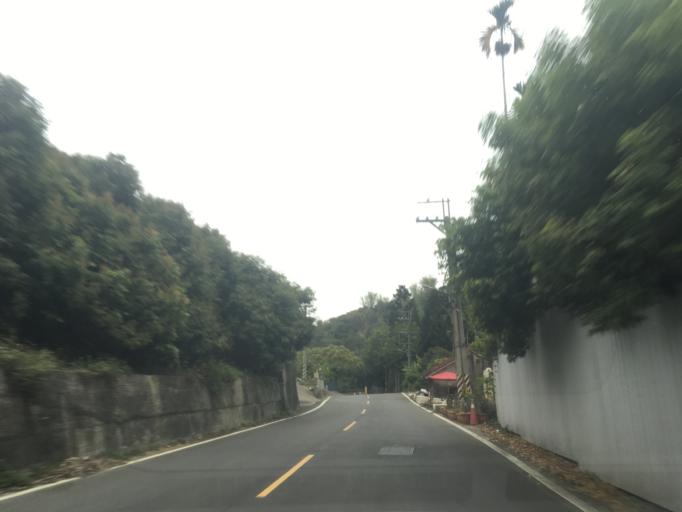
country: TW
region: Taiwan
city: Zhongxing New Village
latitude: 24.0344
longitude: 120.7311
